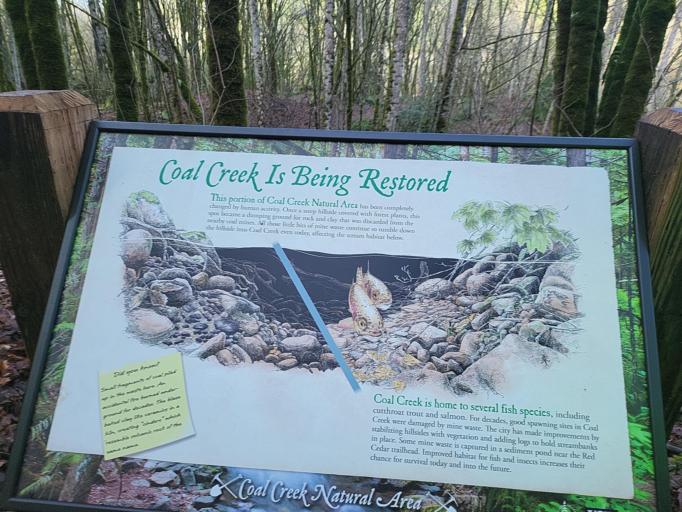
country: US
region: Washington
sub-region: King County
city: Newcastle
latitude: 47.5416
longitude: -122.1465
